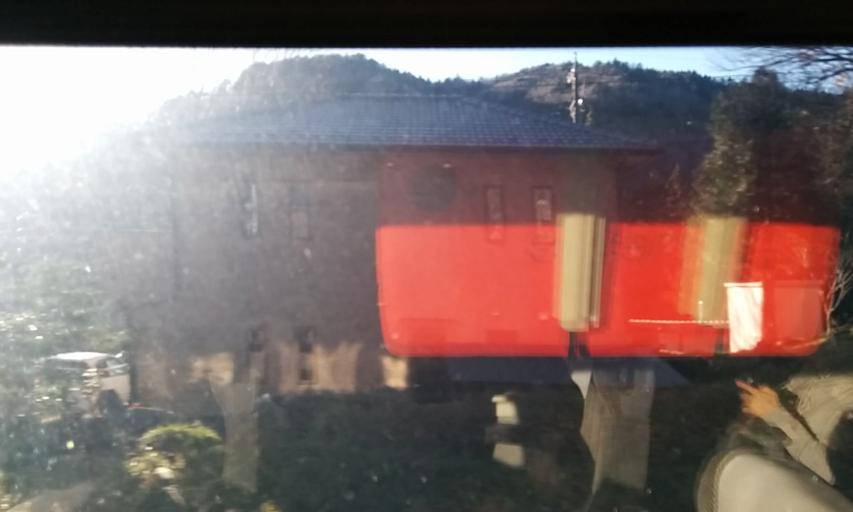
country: JP
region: Nagano
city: Ina
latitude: 35.8132
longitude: 137.6838
